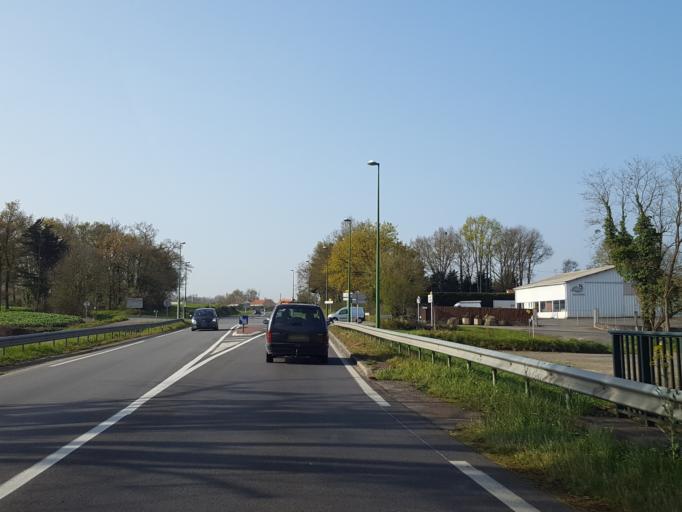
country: FR
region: Pays de la Loire
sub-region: Departement de la Vendee
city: Saint-Philbert-de-Bouaine
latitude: 46.9844
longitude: -1.5176
